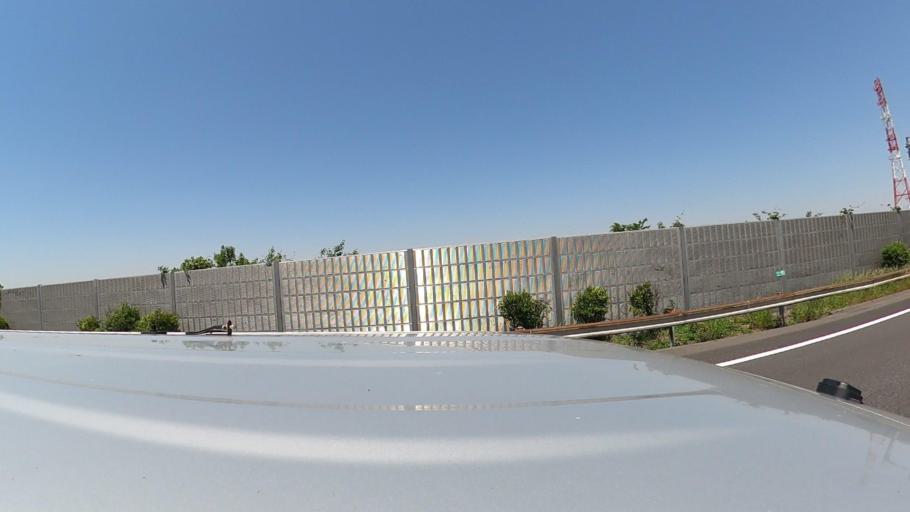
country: JP
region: Ibaraki
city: Mitsukaido
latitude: 35.9864
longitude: 140.0215
